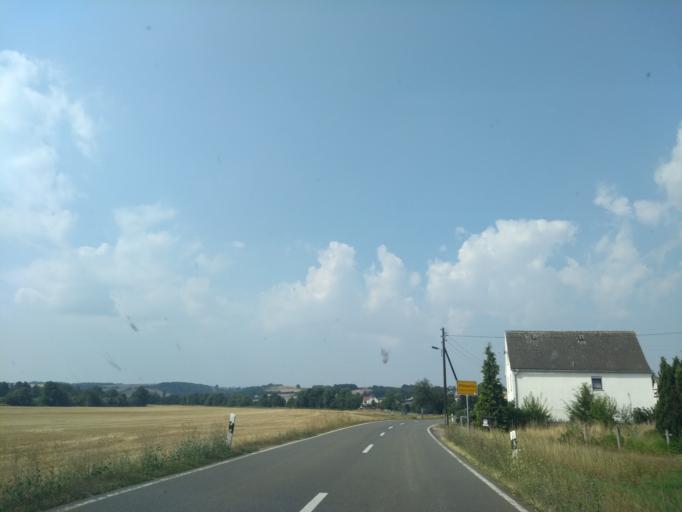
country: DE
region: Saxony-Anhalt
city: Wetterzeube
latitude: 51.0068
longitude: 12.0014
